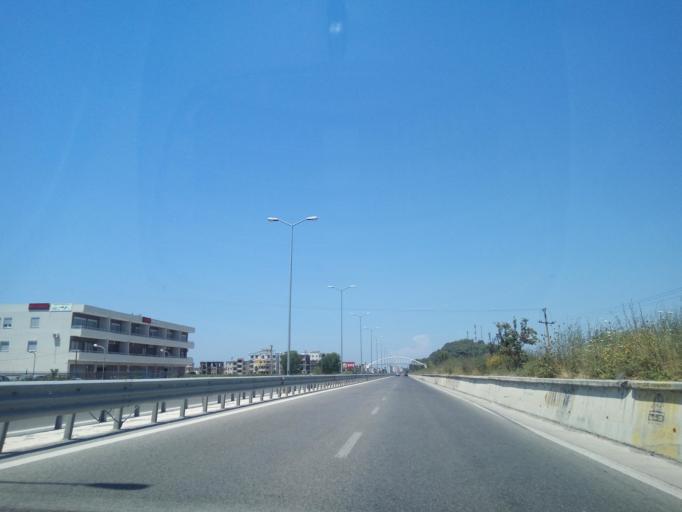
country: AL
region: Tirane
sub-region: Rrethi i Kavajes
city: Golem
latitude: 41.2219
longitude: 19.5284
